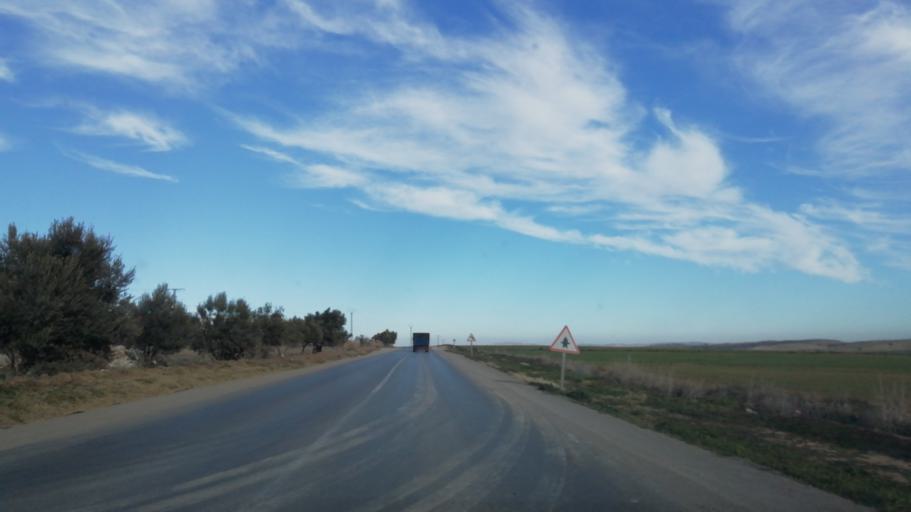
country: DZ
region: Sidi Bel Abbes
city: Sfizef
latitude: 35.2438
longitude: -0.2201
